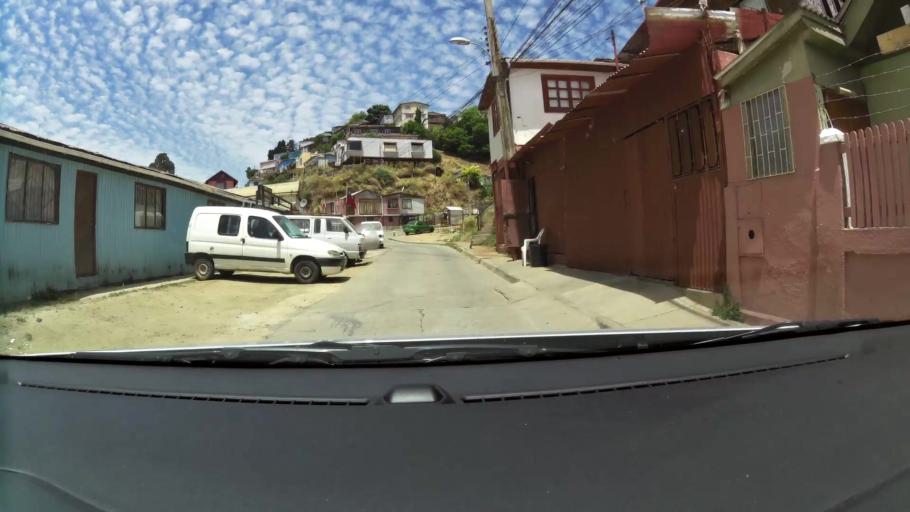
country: CL
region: Valparaiso
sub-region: Provincia de Valparaiso
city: Vina del Mar
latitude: -33.0496
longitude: -71.5705
